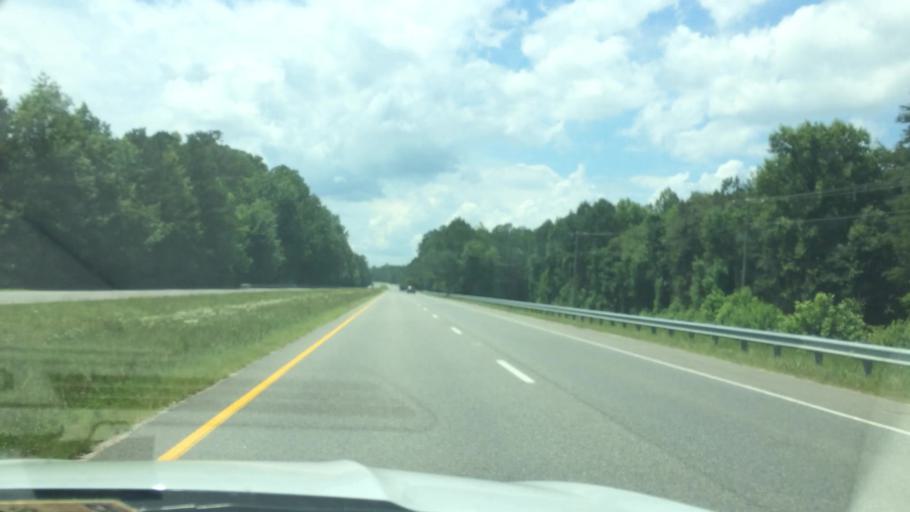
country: US
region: Virginia
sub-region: Middlesex County
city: Saluda
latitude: 37.5636
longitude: -76.6364
